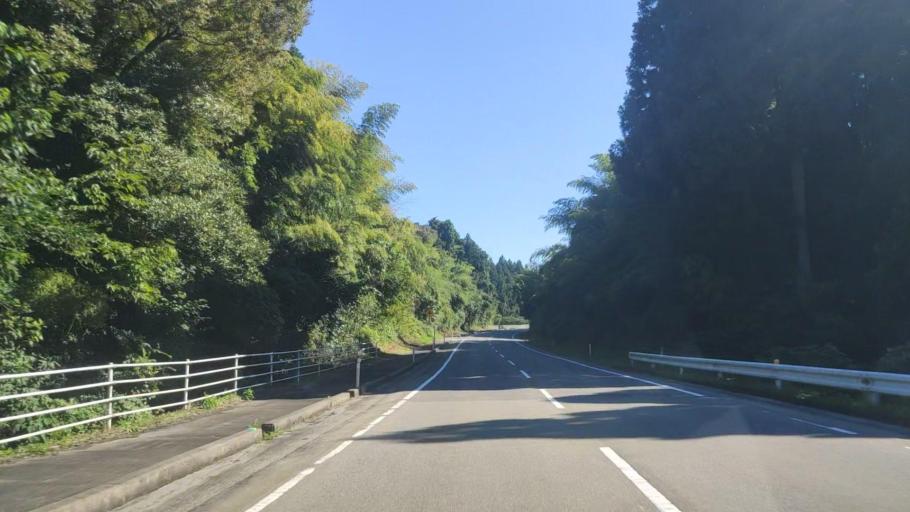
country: JP
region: Ishikawa
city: Nanao
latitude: 37.3767
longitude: 137.2337
